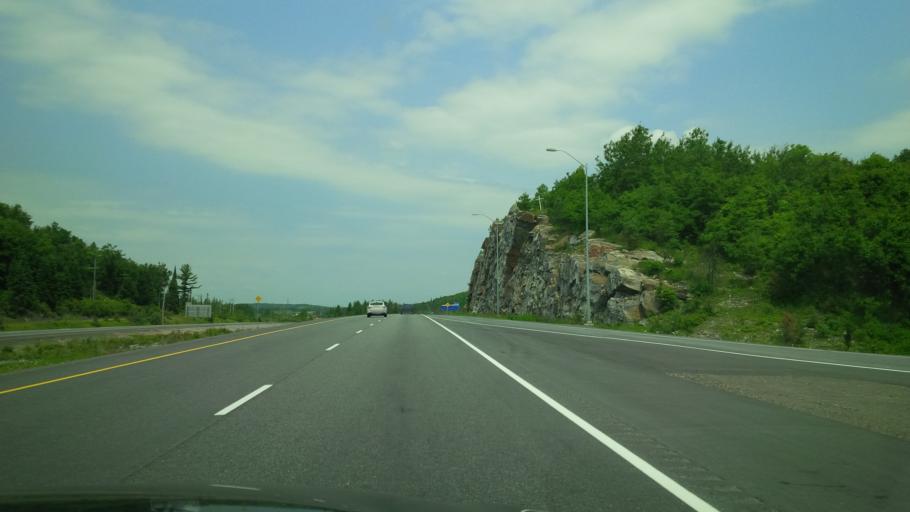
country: CA
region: Ontario
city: Huntsville
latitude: 45.4224
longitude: -79.2375
